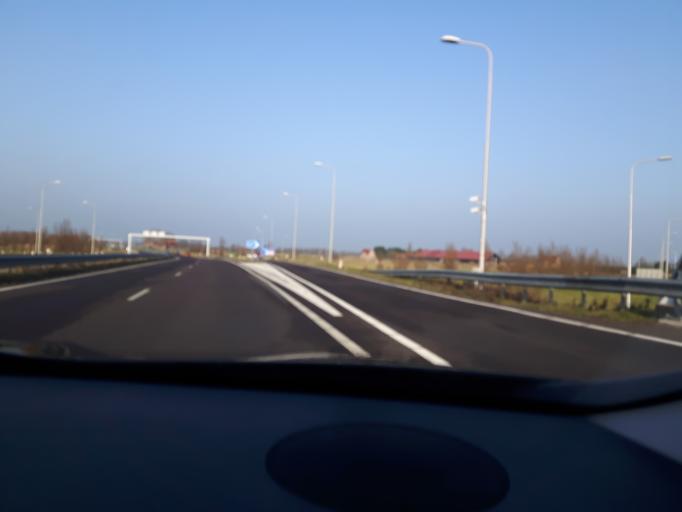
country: NL
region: Zeeland
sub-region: Gemeente Middelburg
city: Middelburg
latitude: 51.5065
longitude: 3.6335
